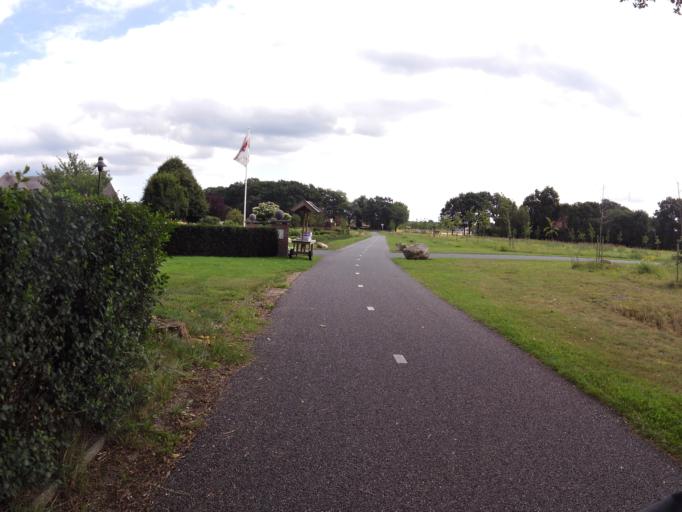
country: NL
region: Drenthe
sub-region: Gemeente Borger-Odoorn
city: Borger
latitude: 52.9257
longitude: 6.7767
